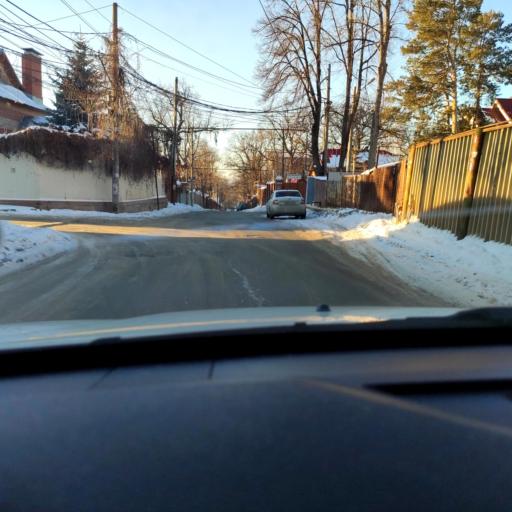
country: RU
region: Samara
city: Samara
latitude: 53.2618
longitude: 50.1919
